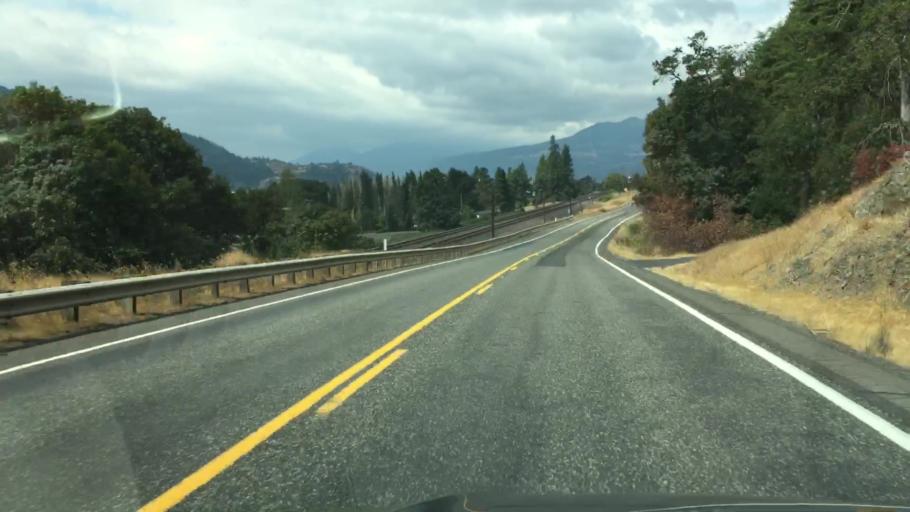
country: US
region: Washington
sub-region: Klickitat County
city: White Salmon
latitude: 45.7039
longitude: -121.4372
